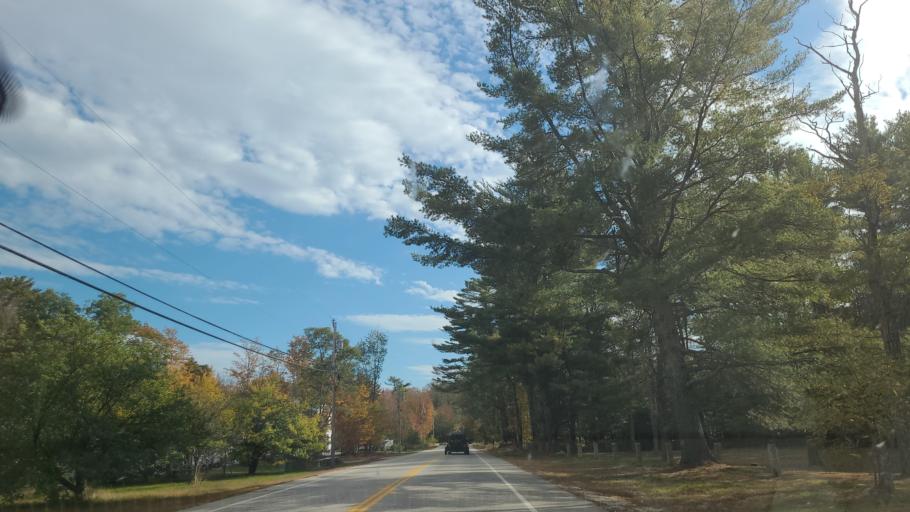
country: US
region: New Hampshire
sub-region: Carroll County
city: Conway
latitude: 44.0041
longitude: -71.1297
